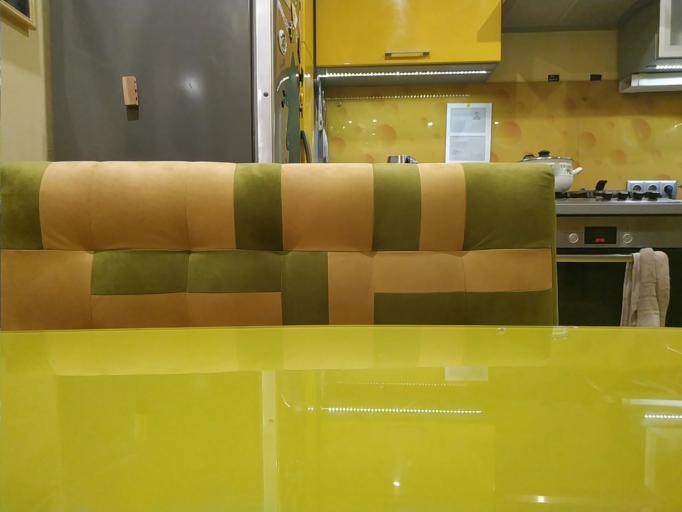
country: RU
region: Murmansk
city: Alakurtti
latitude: 66.1850
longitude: 30.2970
